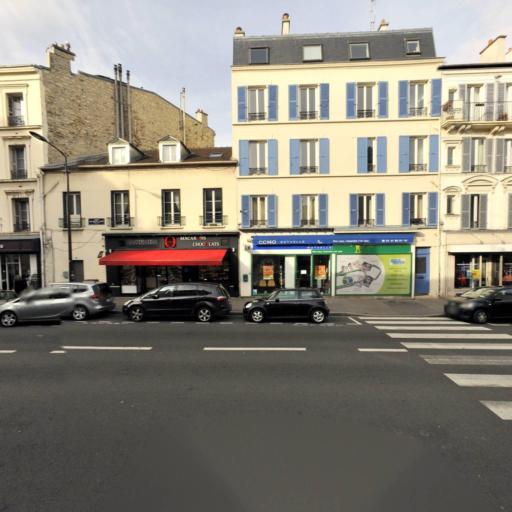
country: FR
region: Ile-de-France
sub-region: Departement des Hauts-de-Seine
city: Boulogne-Billancourt
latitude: 48.8461
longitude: 2.2377
